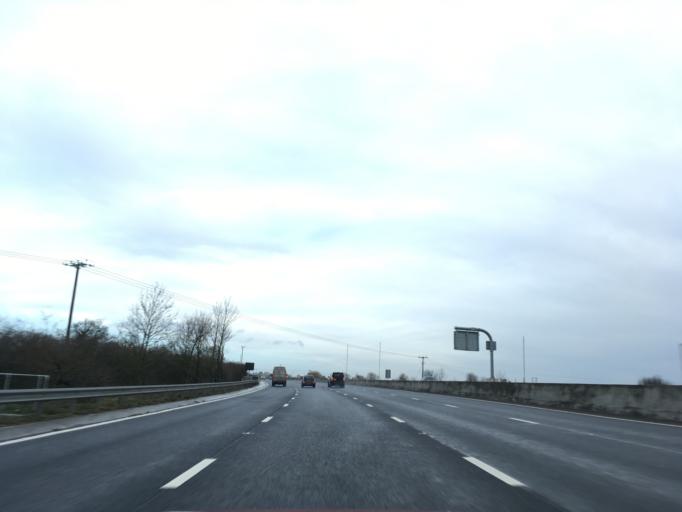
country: GB
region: England
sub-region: Worcestershire
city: Droitwich
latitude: 52.2731
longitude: -2.1228
